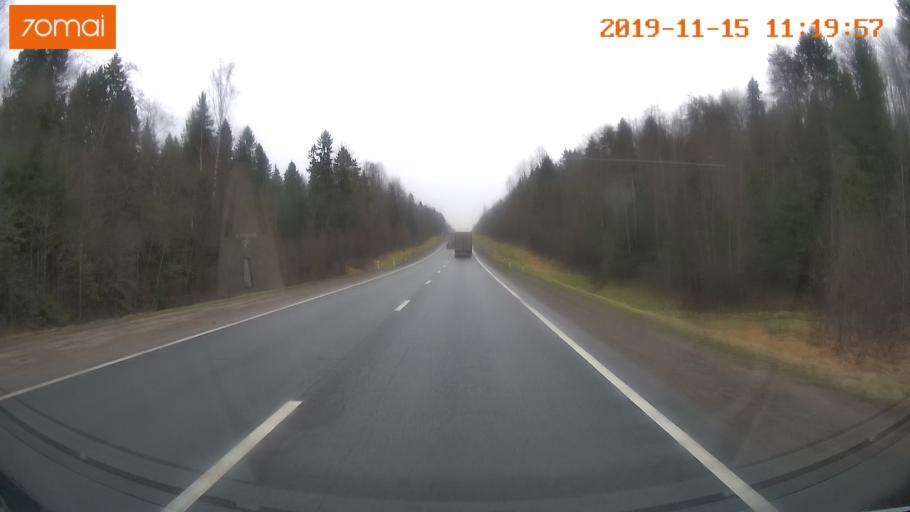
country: RU
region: Vologda
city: Molochnoye
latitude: 59.1402
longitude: 39.3046
